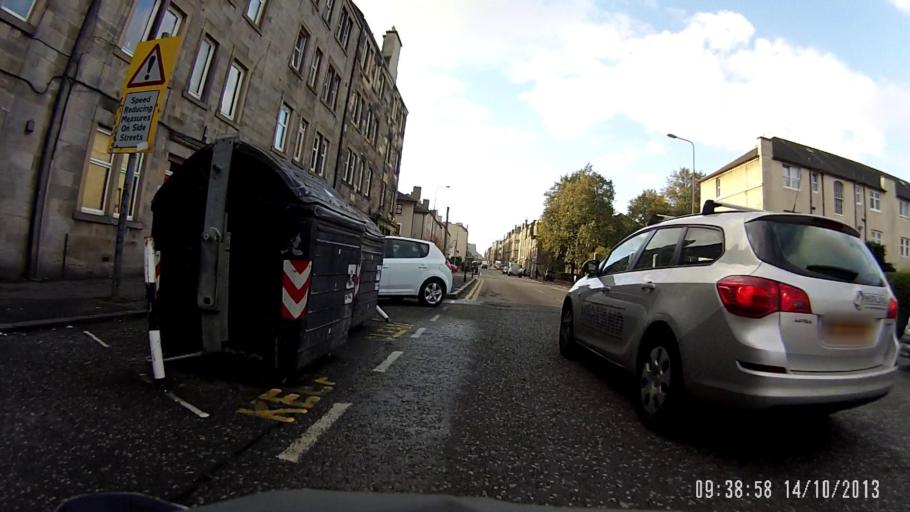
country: GB
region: Scotland
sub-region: West Lothian
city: Seafield
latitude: 55.9648
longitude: -3.1703
